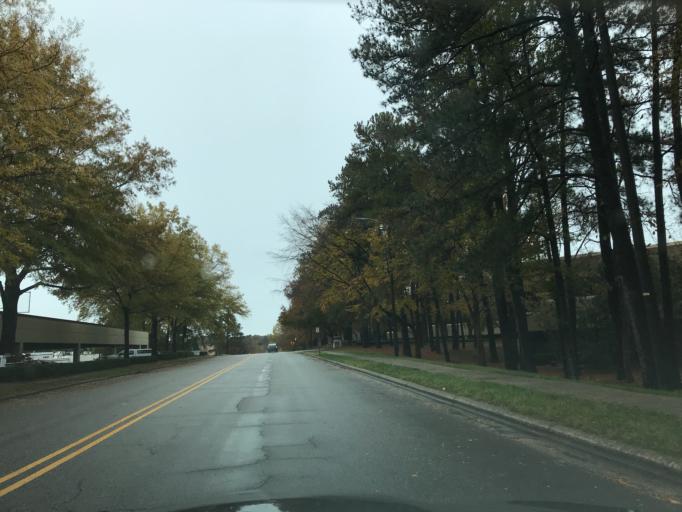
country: US
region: North Carolina
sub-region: Wake County
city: Raleigh
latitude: 35.8424
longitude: -78.6146
